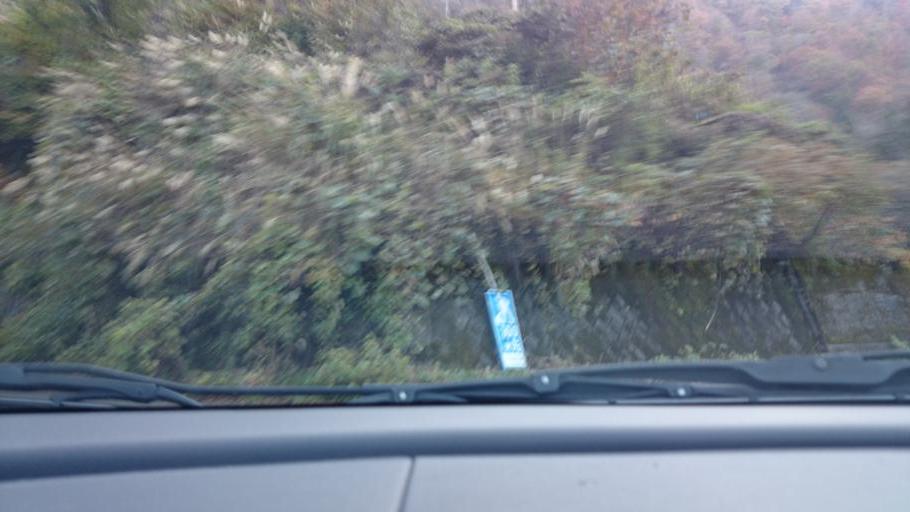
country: JP
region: Fukushima
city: Kitakata
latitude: 37.4619
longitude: 139.5947
